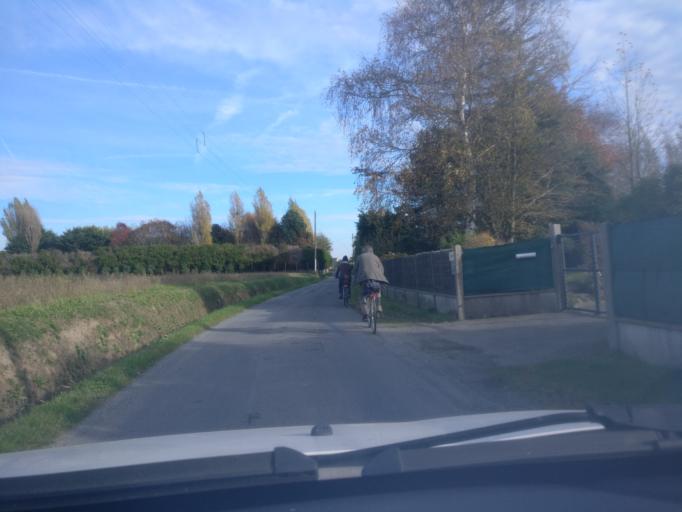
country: FR
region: Brittany
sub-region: Departement d'Ille-et-Vilaine
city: Cancale
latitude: 48.6747
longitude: -1.8695
